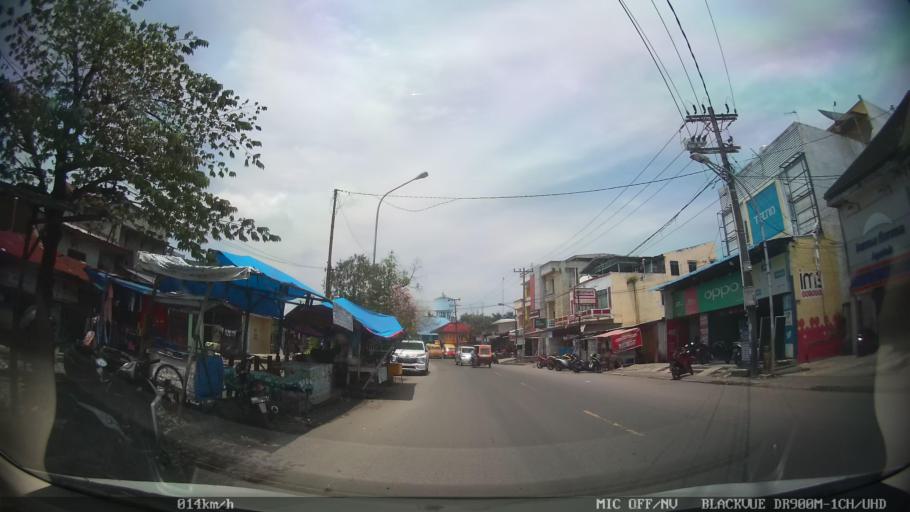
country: ID
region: North Sumatra
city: Belawan
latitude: 3.7826
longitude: 98.6842
